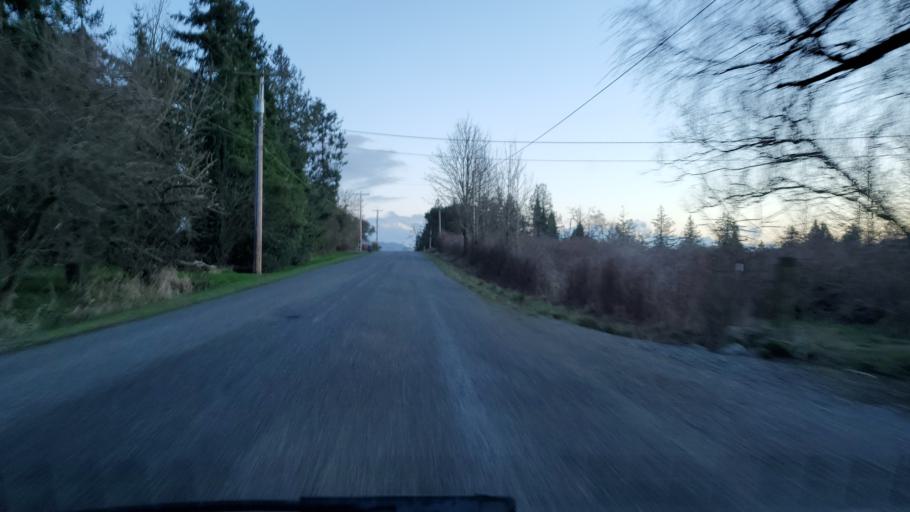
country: US
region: Washington
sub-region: Skagit County
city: Burlington
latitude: 48.4575
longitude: -122.2920
